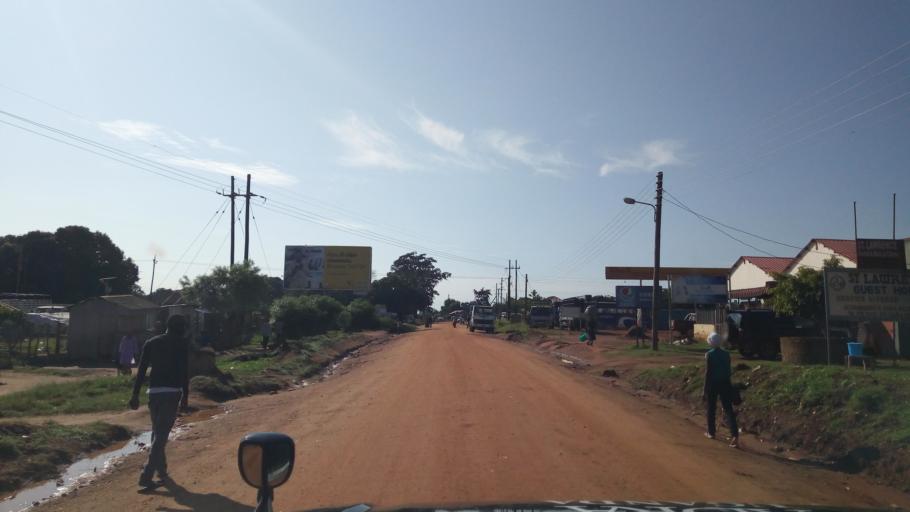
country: UG
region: Northern Region
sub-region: Adjumani District
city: Adjumani
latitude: 3.3795
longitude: 31.7917
